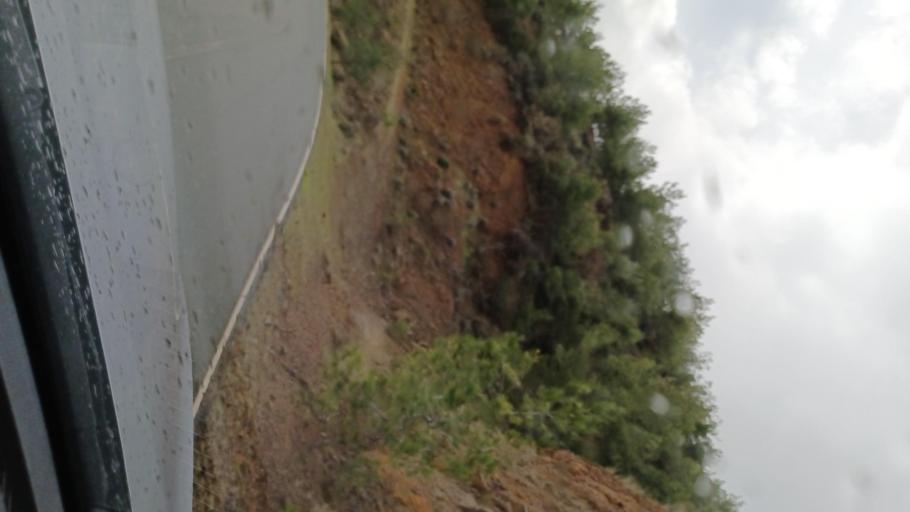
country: CY
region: Lefkosia
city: Lefka
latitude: 35.0985
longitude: 32.7574
